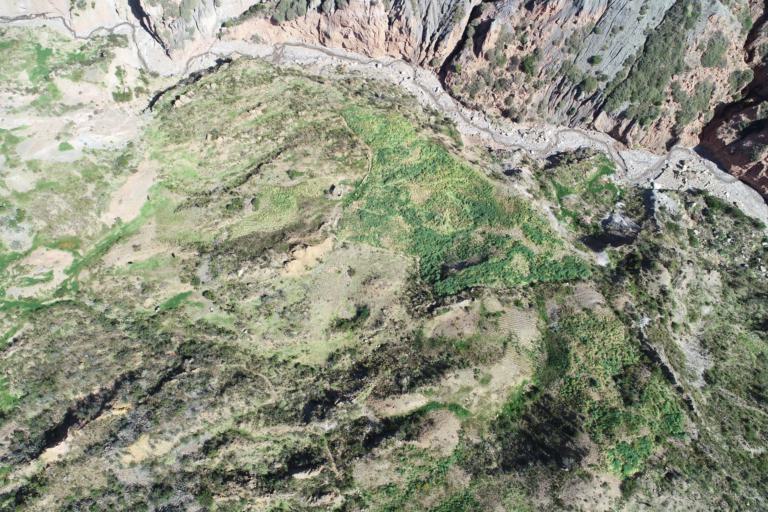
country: BO
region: La Paz
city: La Paz
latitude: -16.5583
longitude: -67.9888
